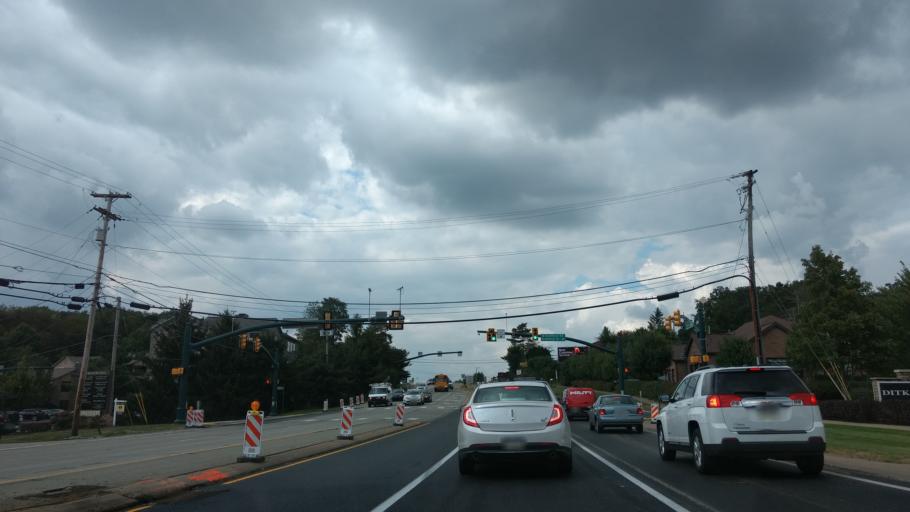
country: US
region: Pennsylvania
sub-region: Allegheny County
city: Bradford Woods
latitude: 40.6422
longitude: -80.0671
